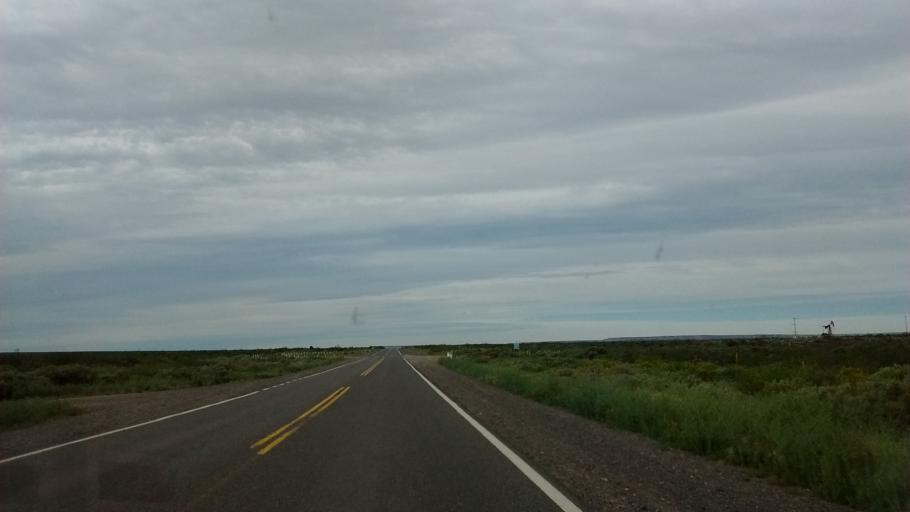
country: AR
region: Rio Negro
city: Catriel
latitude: -38.0517
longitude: -67.9199
